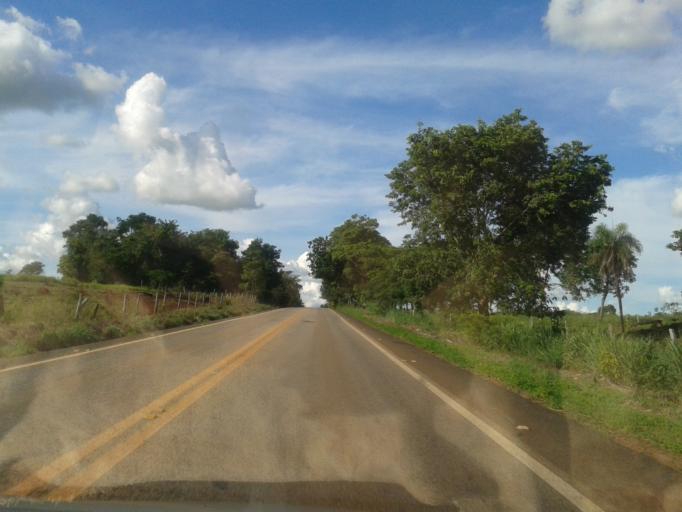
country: BR
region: Goias
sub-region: Mozarlandia
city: Mozarlandia
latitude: -14.6441
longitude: -50.5199
